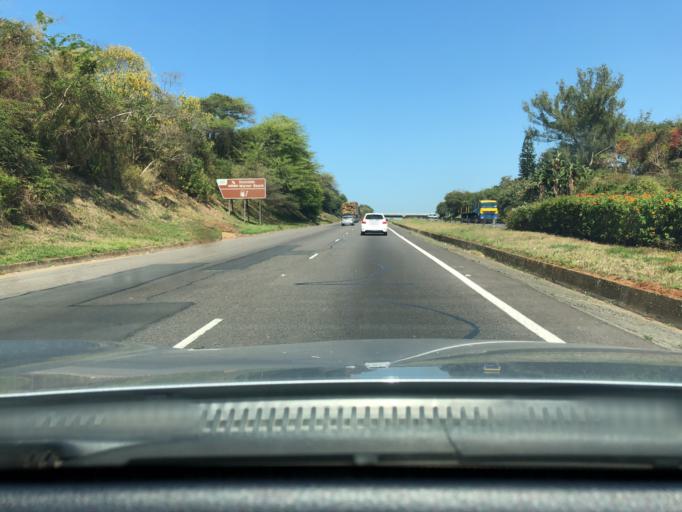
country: ZA
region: KwaZulu-Natal
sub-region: eThekwini Metropolitan Municipality
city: Umkomaas
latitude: -30.0614
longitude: 30.8774
